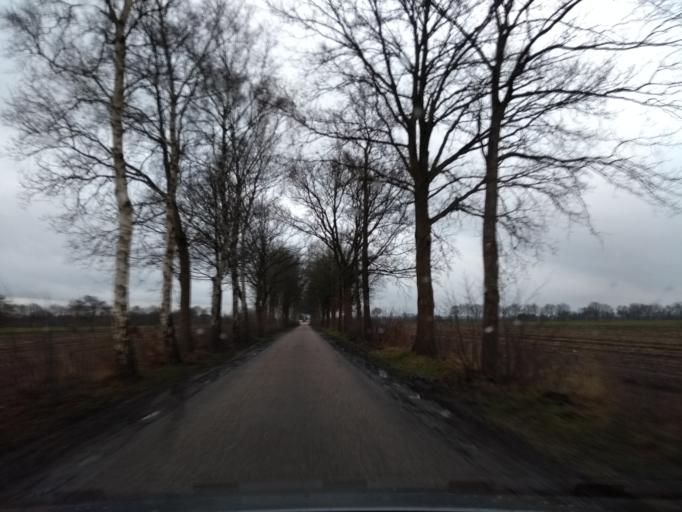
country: NL
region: Drenthe
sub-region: Gemeente De Wolden
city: Ruinen
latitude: 52.7324
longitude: 6.3433
